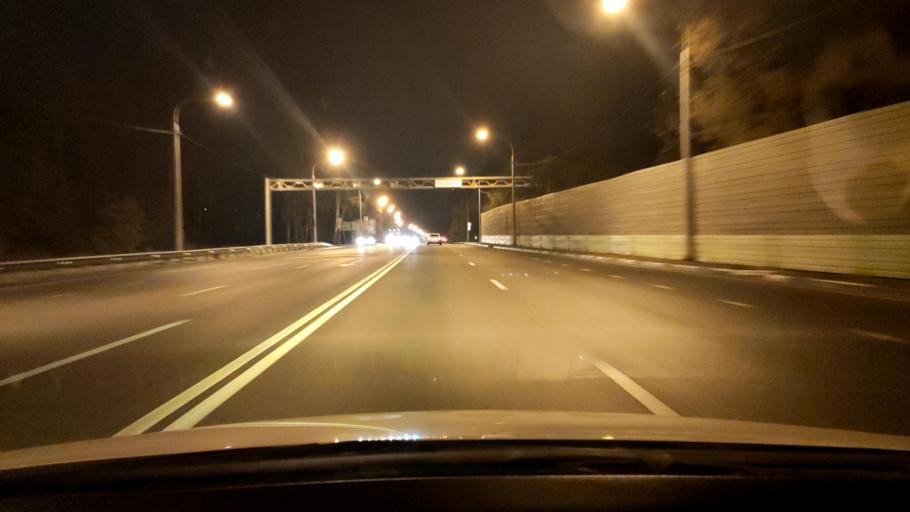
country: RU
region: Voronezj
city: Pridonskoy
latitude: 51.6852
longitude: 39.1153
